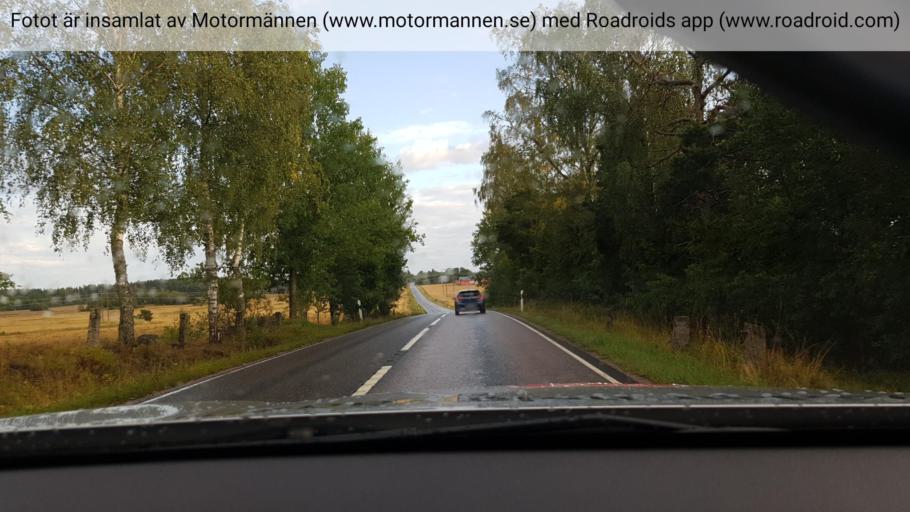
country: SE
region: Stockholm
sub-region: Norrtalje Kommun
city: Norrtalje
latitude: 59.7960
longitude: 18.6589
